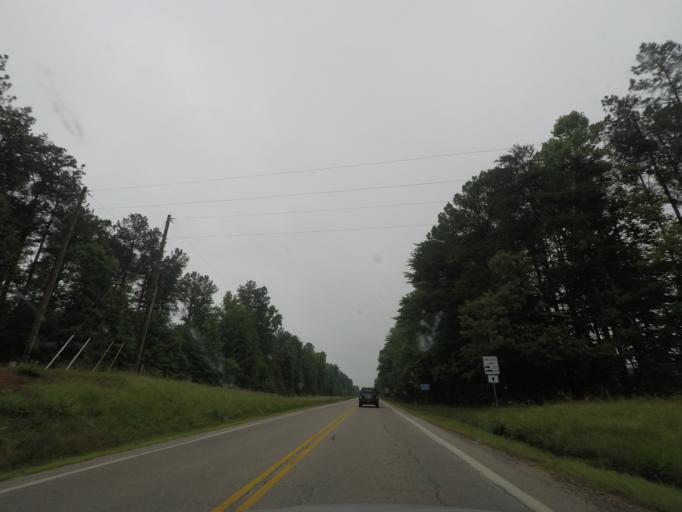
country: US
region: Virginia
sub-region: Prince Edward County
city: Hampden Sydney
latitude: 37.0861
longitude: -78.4751
